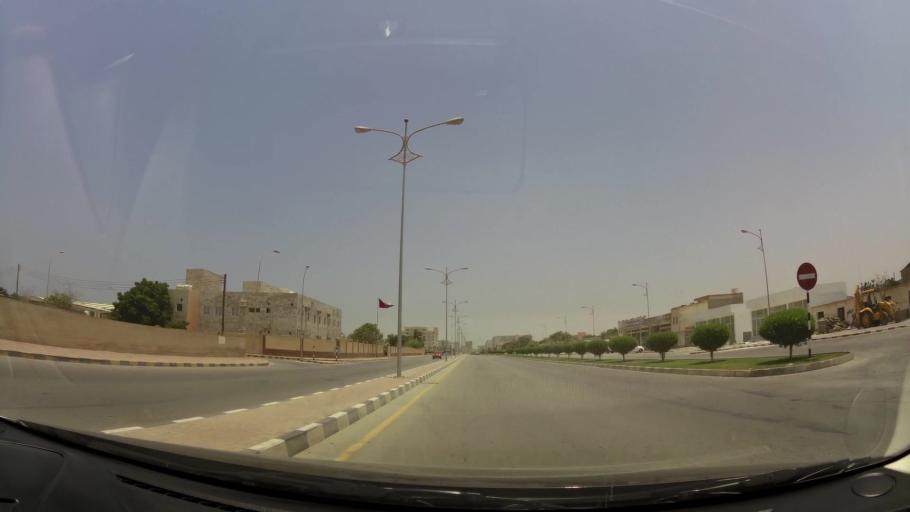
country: OM
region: Zufar
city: Salalah
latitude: 17.0209
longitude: 54.1187
